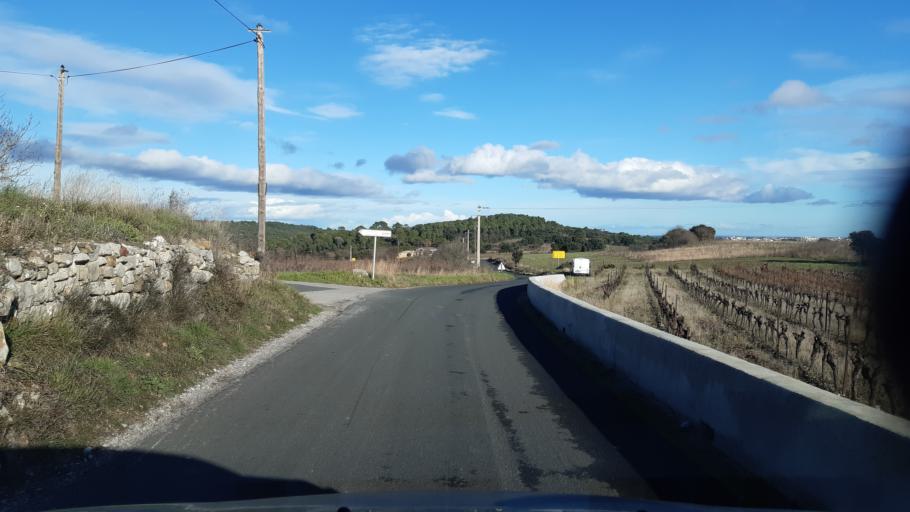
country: FR
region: Languedoc-Roussillon
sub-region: Departement de l'Herault
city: Murviel-les-Montpellier
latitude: 43.6104
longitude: 3.7385
